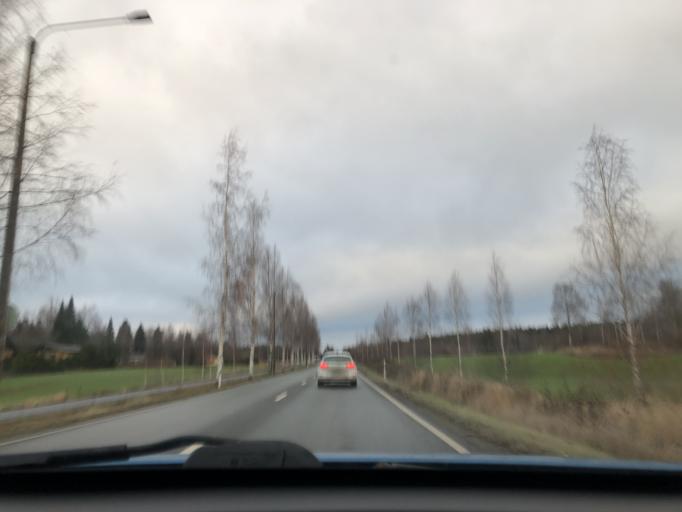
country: FI
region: Pirkanmaa
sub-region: Tampere
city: Kangasala
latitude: 61.4858
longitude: 24.0549
